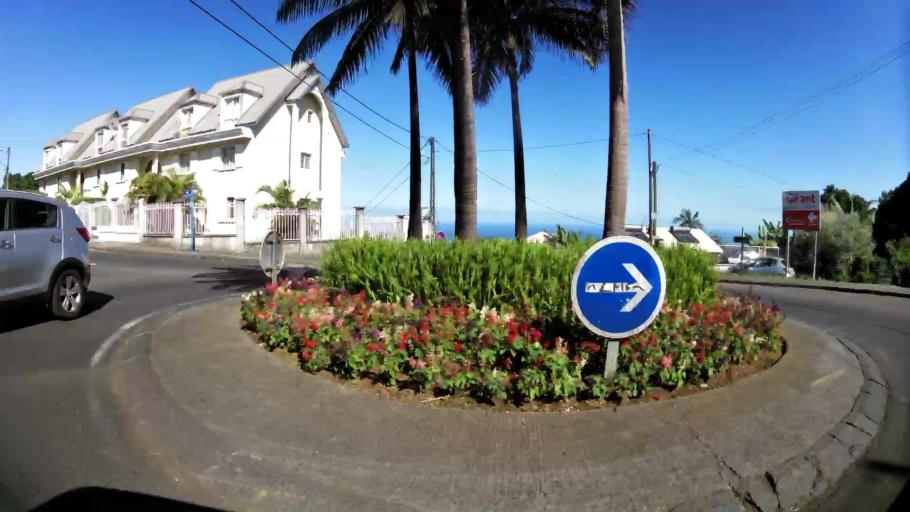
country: RE
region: Reunion
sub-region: Reunion
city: Le Tampon
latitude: -21.2674
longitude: 55.5127
